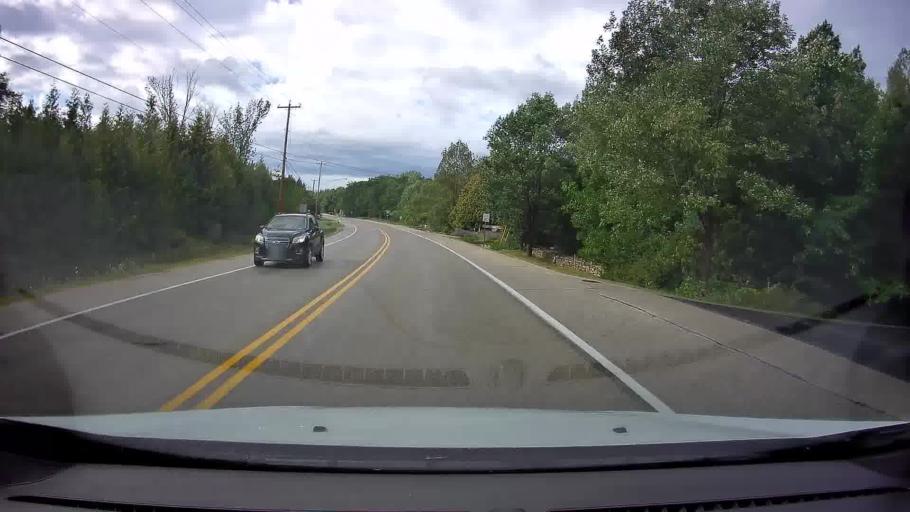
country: US
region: Wisconsin
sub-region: Door County
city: Sturgeon Bay
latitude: 45.0588
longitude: -87.2779
